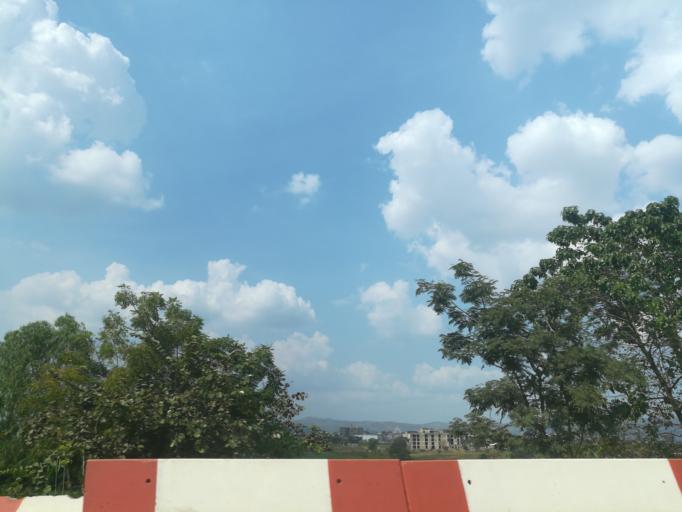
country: NG
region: Abuja Federal Capital Territory
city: Abuja
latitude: 9.0797
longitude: 7.4238
